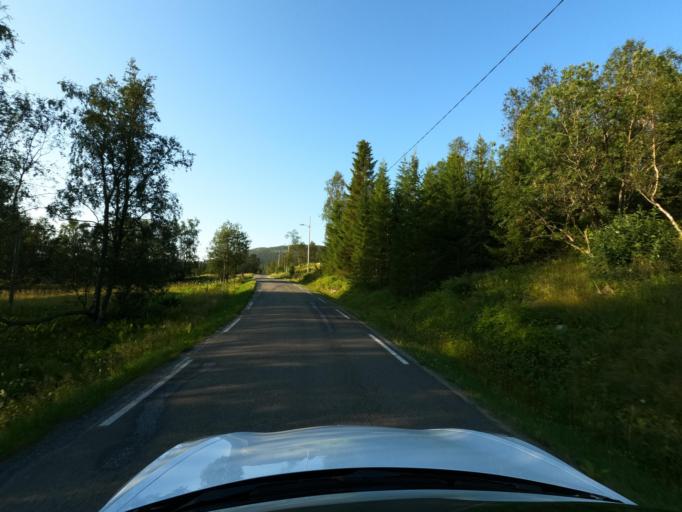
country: NO
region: Nordland
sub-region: Ballangen
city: Ballangen
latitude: 68.5243
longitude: 16.7653
